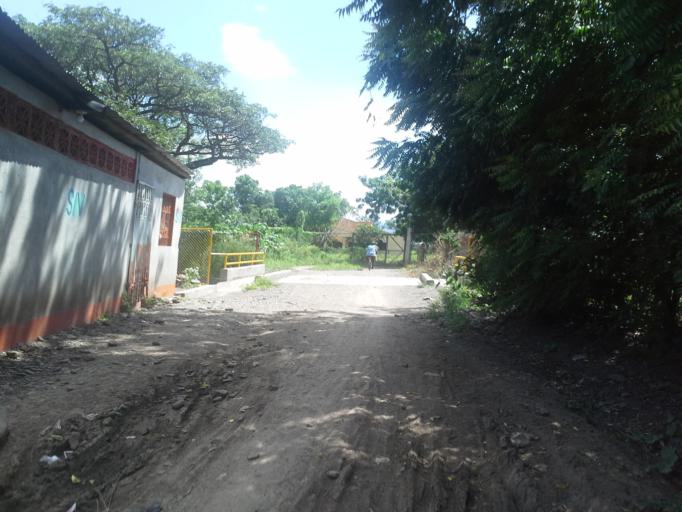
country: NI
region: Matagalpa
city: Ciudad Dario
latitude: 12.8587
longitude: -86.0976
